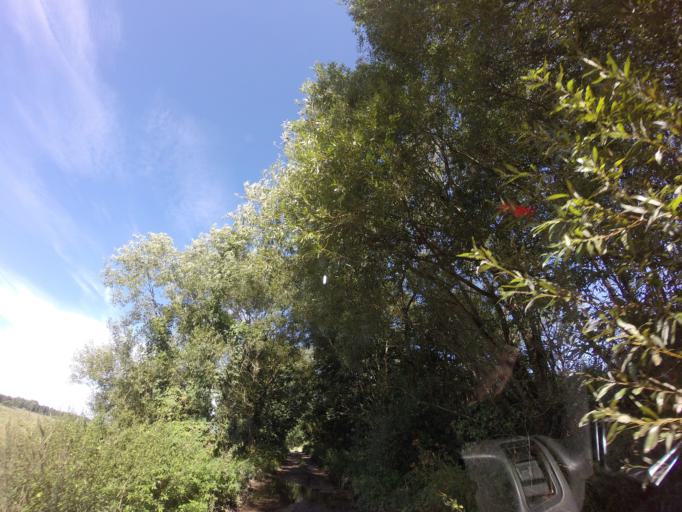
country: PL
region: West Pomeranian Voivodeship
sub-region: Powiat choszczenski
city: Recz
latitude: 53.1996
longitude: 15.5021
